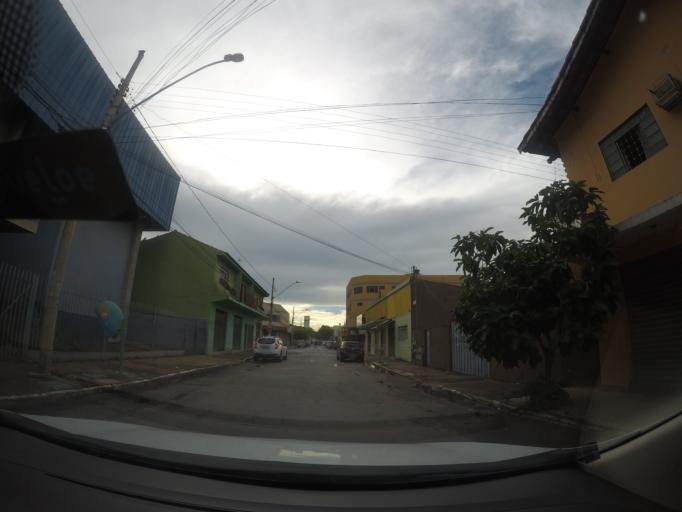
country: BR
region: Goias
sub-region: Goiania
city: Goiania
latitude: -16.6668
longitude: -49.2897
